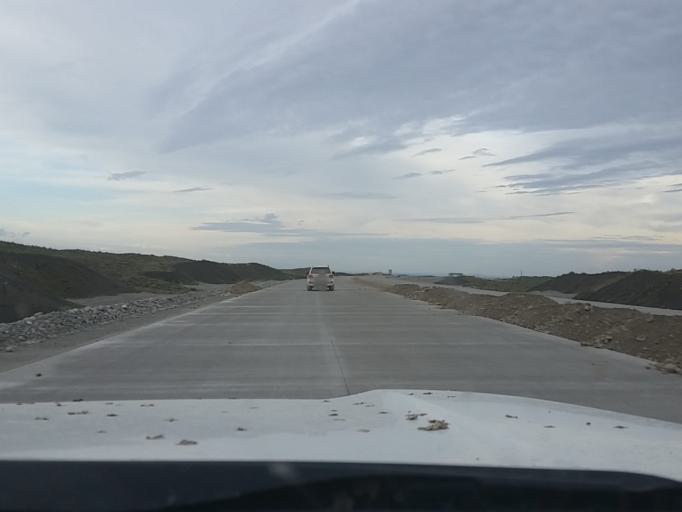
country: KZ
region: Almaty Oblysy
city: Zharkent
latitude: 44.1742
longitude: 80.3330
